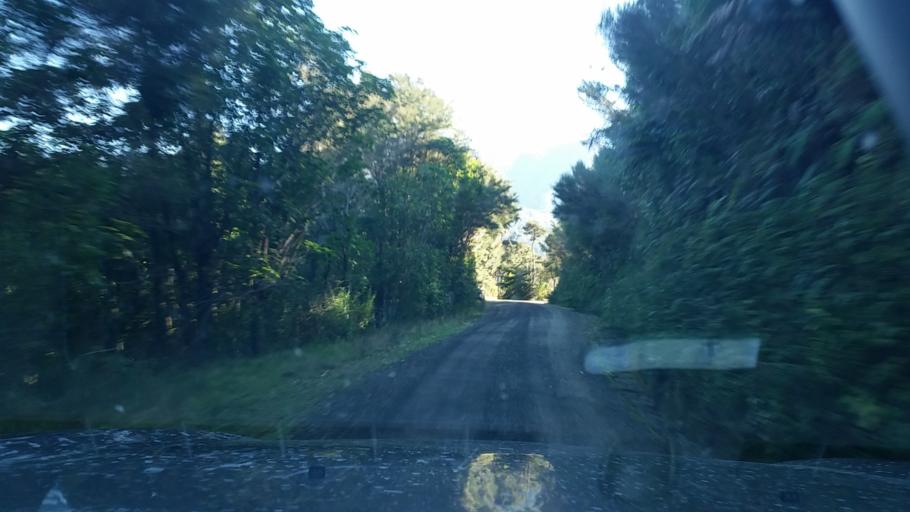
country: NZ
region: Marlborough
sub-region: Marlborough District
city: Picton
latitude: -41.1803
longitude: 173.9734
